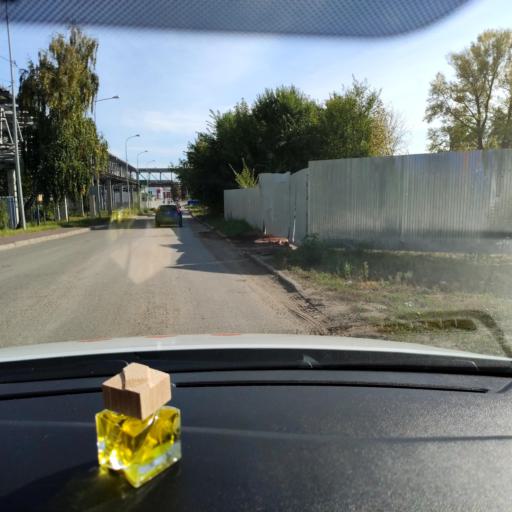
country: RU
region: Tatarstan
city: Staroye Arakchino
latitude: 55.8377
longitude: 49.0483
